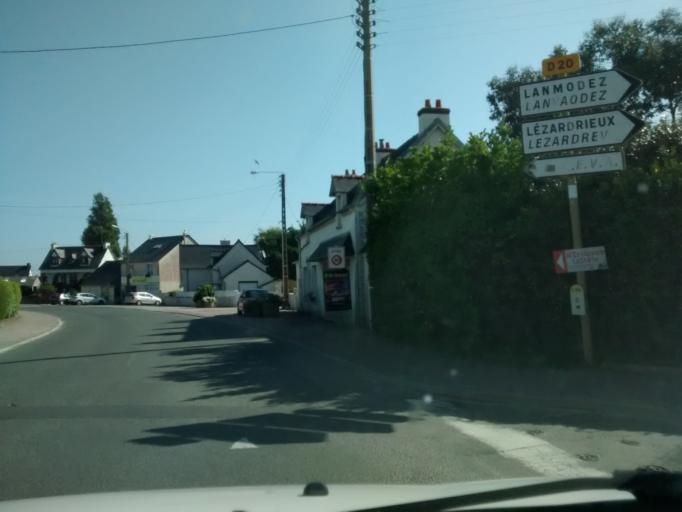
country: FR
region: Brittany
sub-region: Departement des Cotes-d'Armor
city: Pleubian
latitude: 48.8582
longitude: -3.1058
